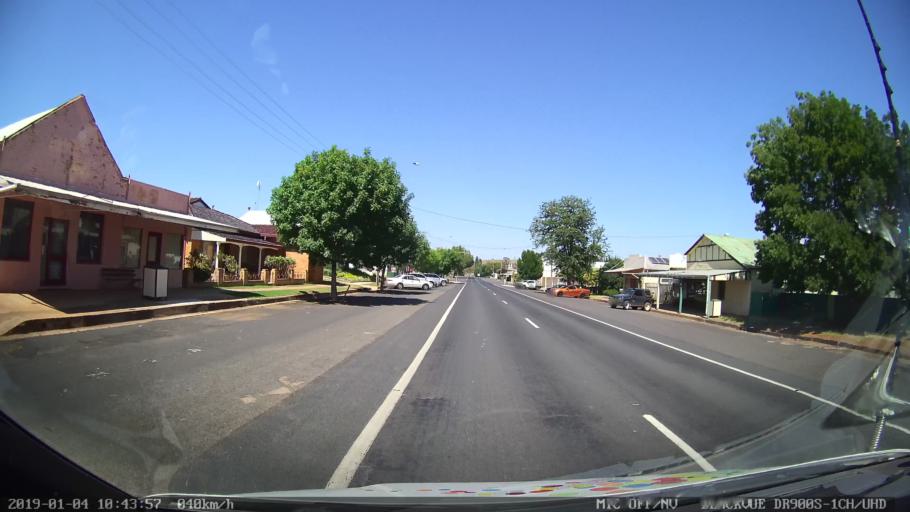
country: AU
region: New South Wales
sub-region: Cabonne
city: Molong
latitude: -33.2863
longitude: 148.7400
